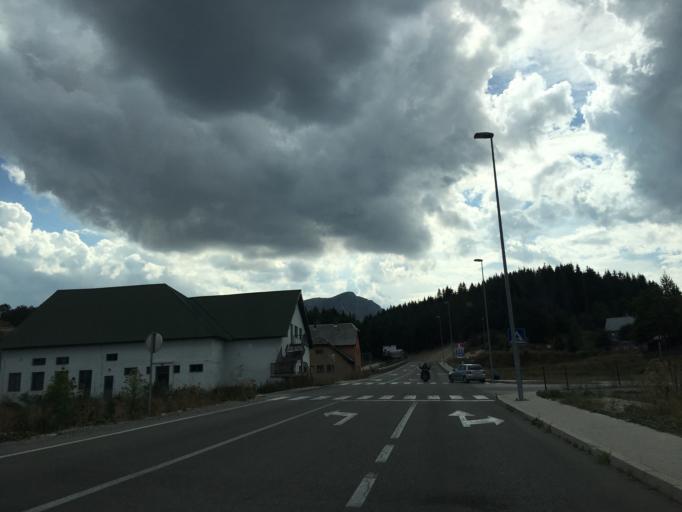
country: ME
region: Opstina Zabljak
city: Zabljak
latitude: 43.1517
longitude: 19.1291
